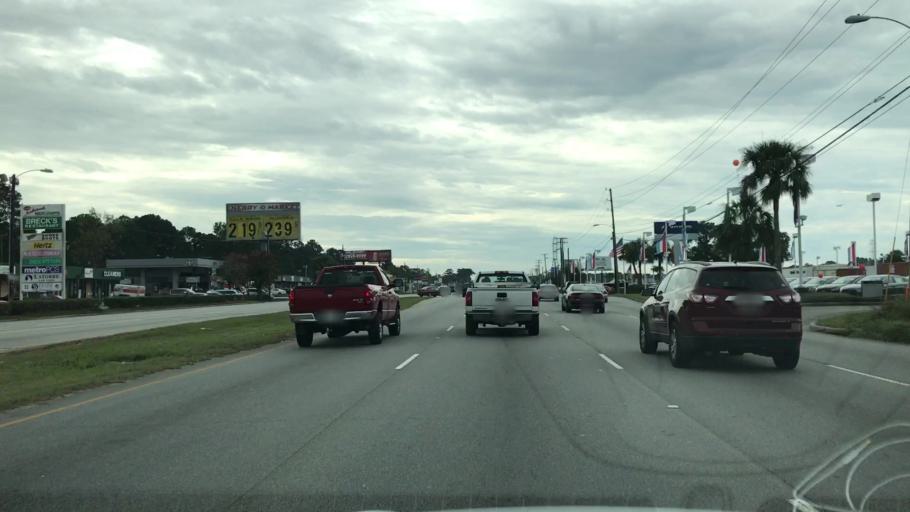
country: US
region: South Carolina
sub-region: Berkeley County
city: Goose Creek
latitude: 32.9618
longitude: -80.0438
